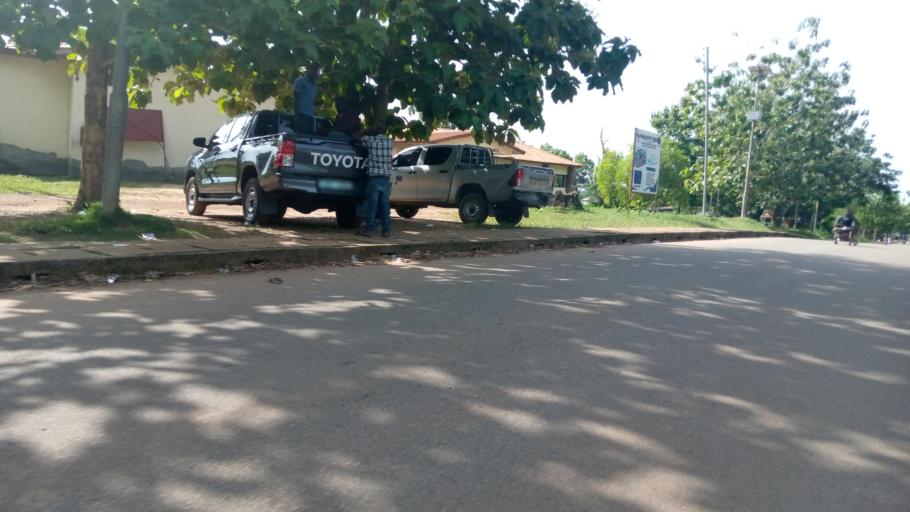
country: SL
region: Southern Province
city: Pujehun
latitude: 7.3525
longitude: -11.7202
